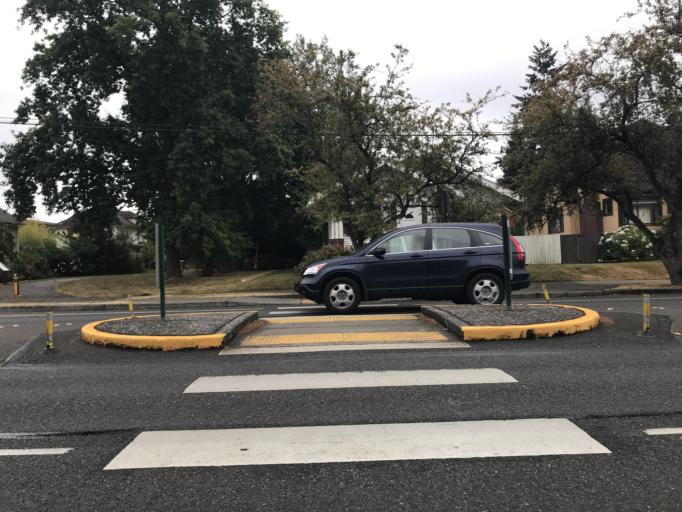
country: US
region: Washington
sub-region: Whatcom County
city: Bellingham
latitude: 48.7593
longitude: -122.4894
